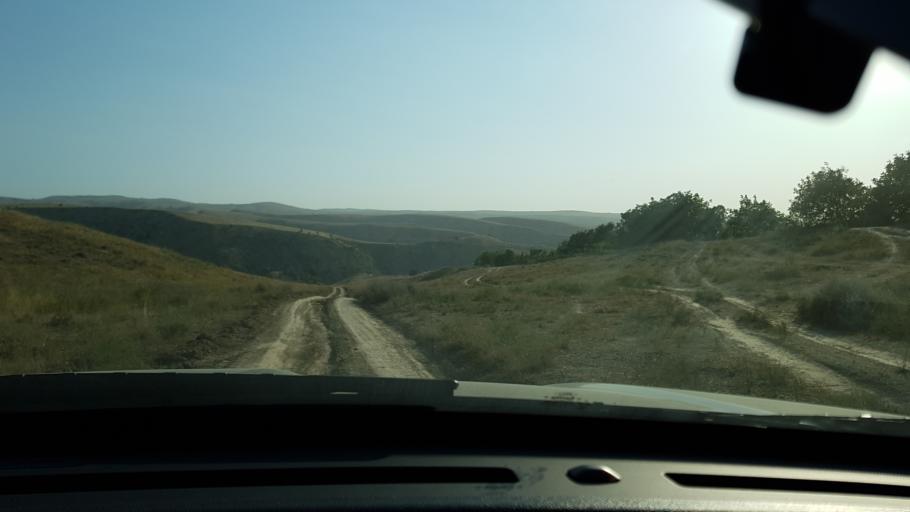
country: TM
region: Ahal
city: Baharly
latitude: 38.4095
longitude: 56.9133
